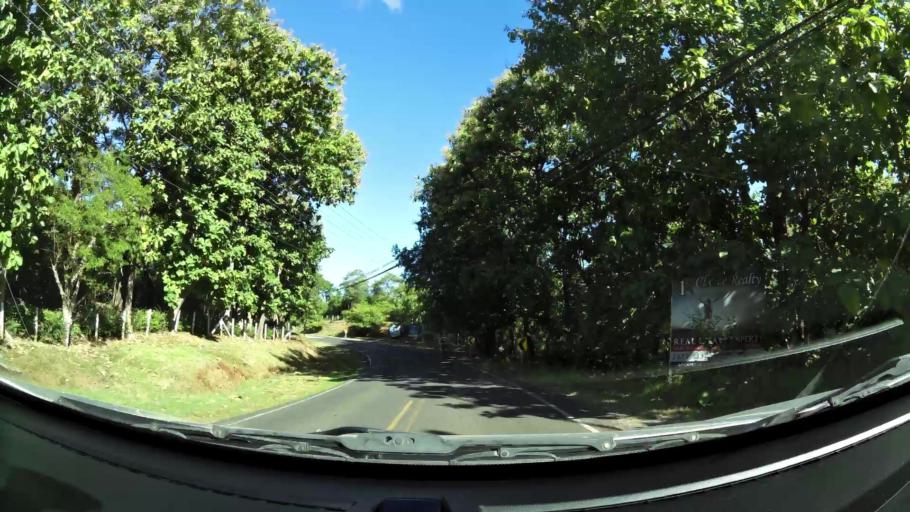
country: CR
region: Guanacaste
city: Sardinal
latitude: 10.3978
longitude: -85.7917
